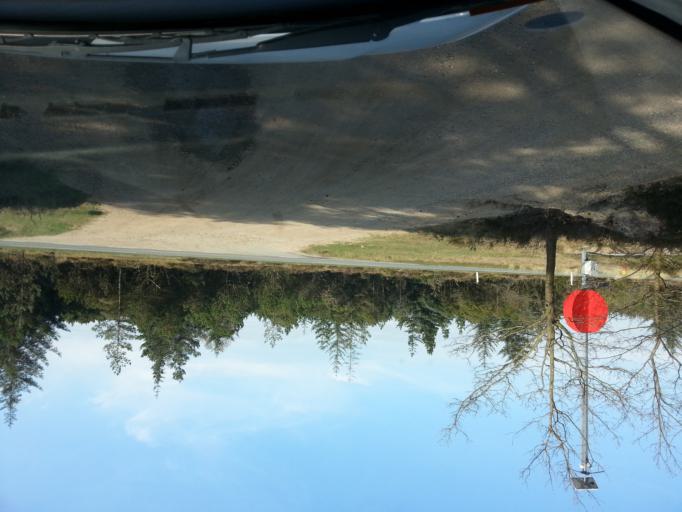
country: DK
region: South Denmark
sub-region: Varde Kommune
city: Oksbol
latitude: 55.5669
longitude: 8.1800
